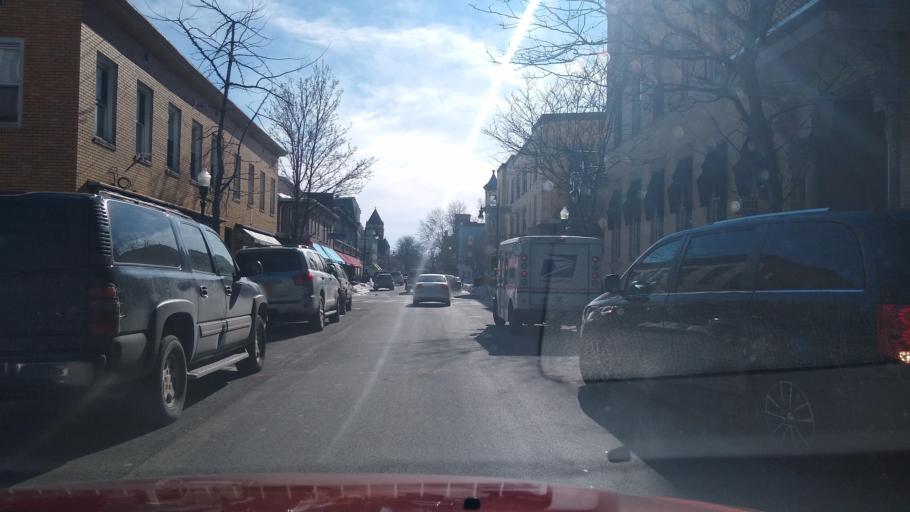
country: US
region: New York
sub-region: Ulster County
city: Kingston
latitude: 41.9343
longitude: -74.0190
